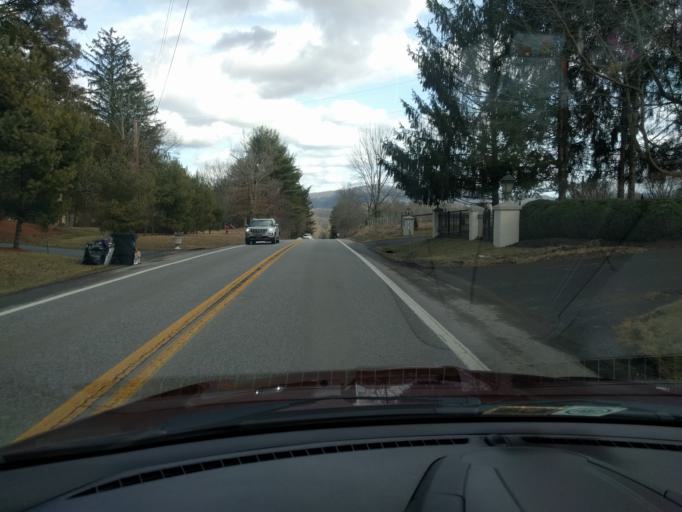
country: US
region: West Virginia
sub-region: Greenbrier County
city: Lewisburg
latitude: 37.7939
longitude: -80.4283
